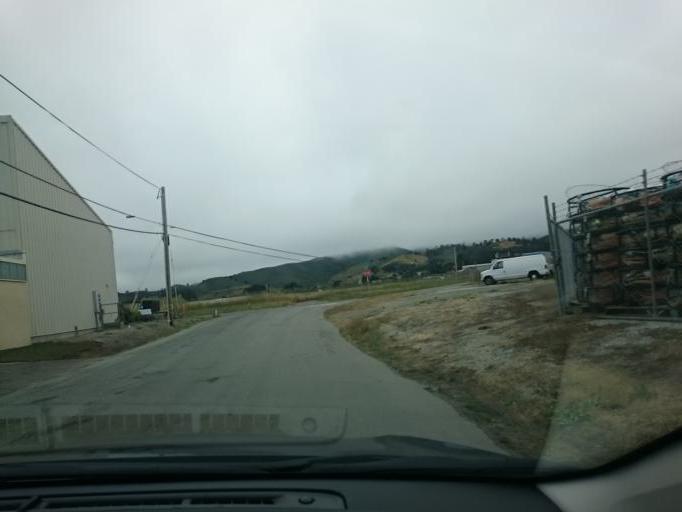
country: US
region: California
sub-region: San Mateo County
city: El Granada
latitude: 37.5047
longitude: -122.4932
